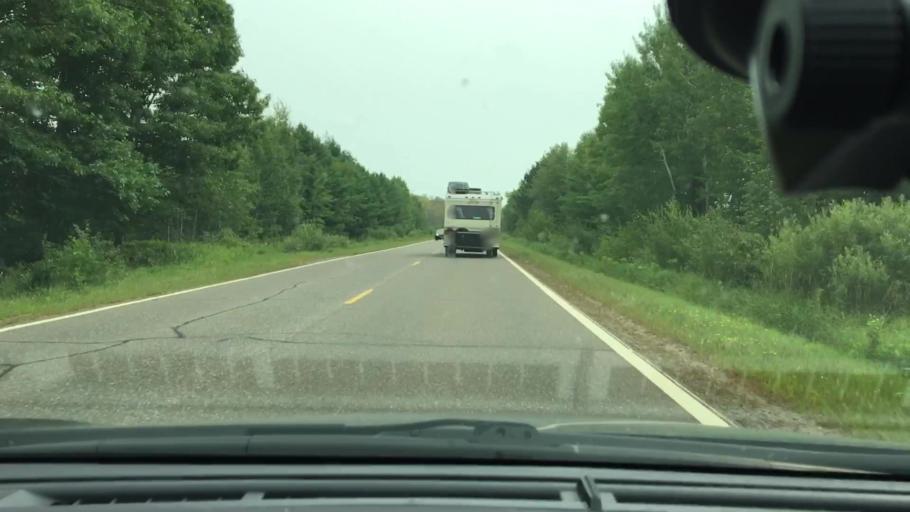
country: US
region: Minnesota
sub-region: Aitkin County
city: Aitkin
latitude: 46.4026
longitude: -93.7575
